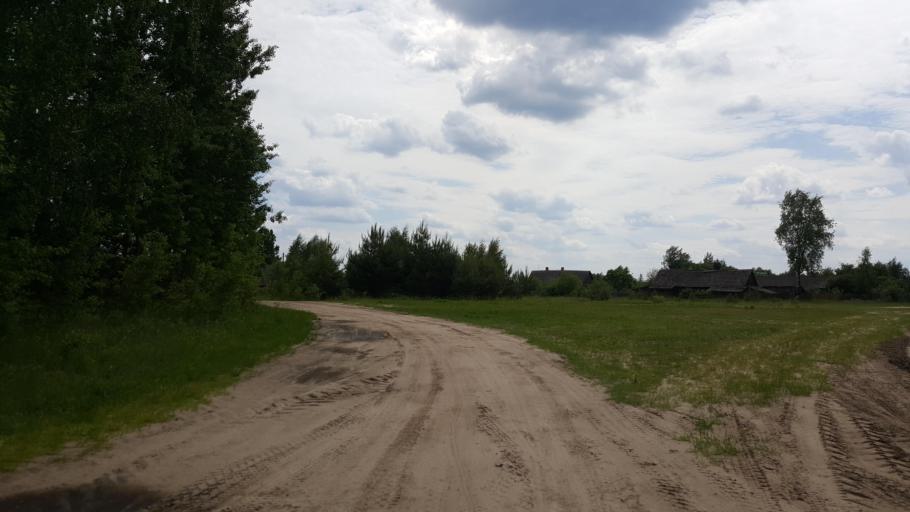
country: PL
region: Podlasie
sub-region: Powiat hajnowski
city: Bialowieza
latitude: 52.6720
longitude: 24.0715
